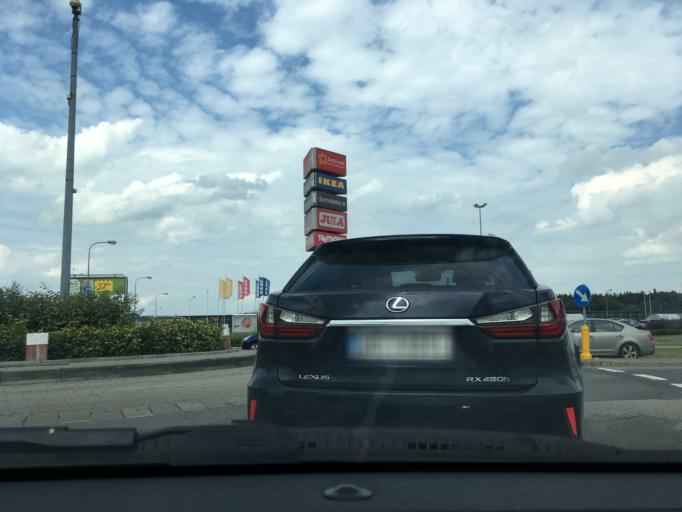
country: PL
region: Masovian Voivodeship
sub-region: Powiat wolominski
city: Zabki
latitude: 52.3058
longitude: 21.0806
